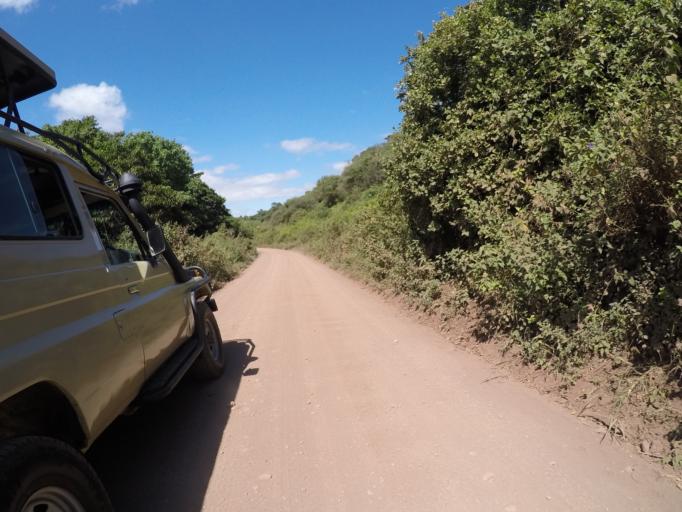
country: TZ
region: Arusha
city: Mto wa Mbu
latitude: -3.3848
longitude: 35.8280
